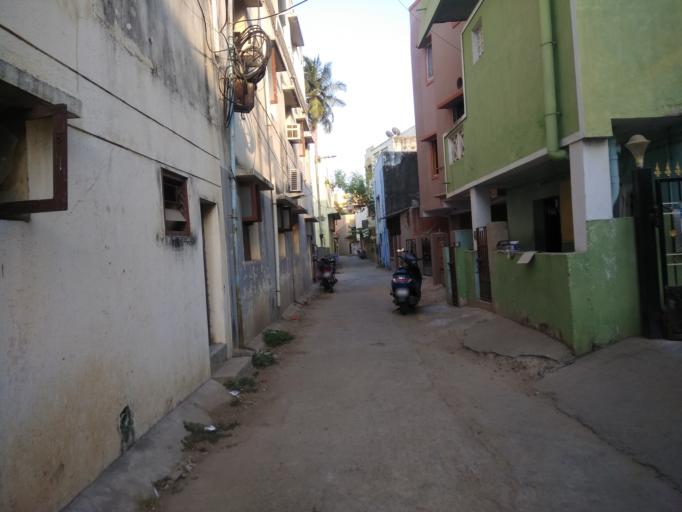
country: IN
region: Tamil Nadu
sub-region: Chennai
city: Chetput
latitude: 13.0759
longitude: 80.2055
